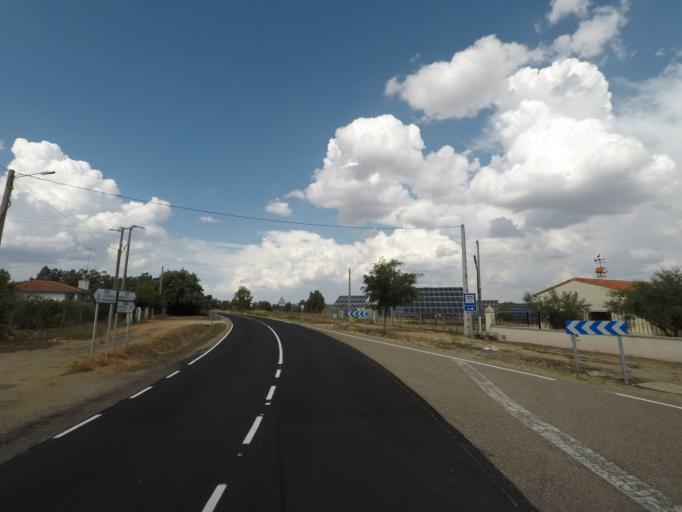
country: ES
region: Castille and Leon
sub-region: Provincia de Zamora
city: Fermoselle
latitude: 41.3149
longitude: -6.3071
